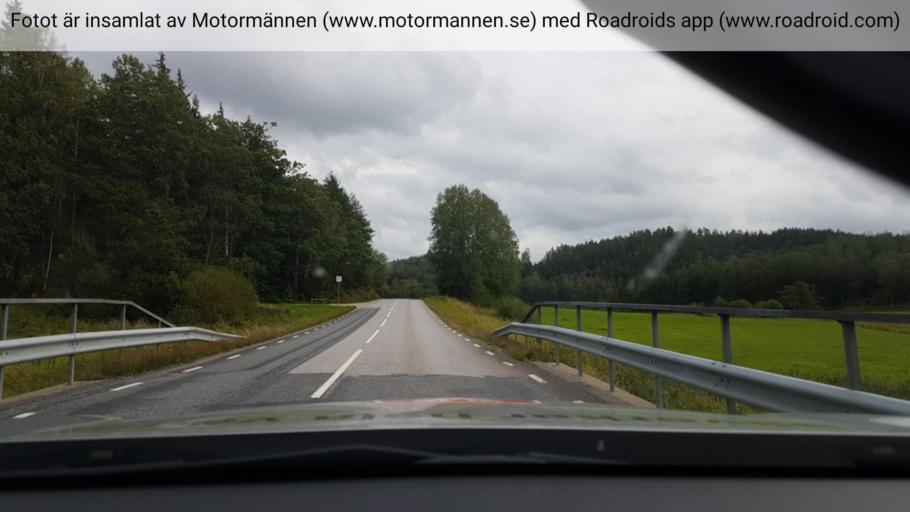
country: SE
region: Vaestra Goetaland
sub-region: Sotenas Kommun
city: Hunnebostrand
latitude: 58.5503
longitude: 11.4112
